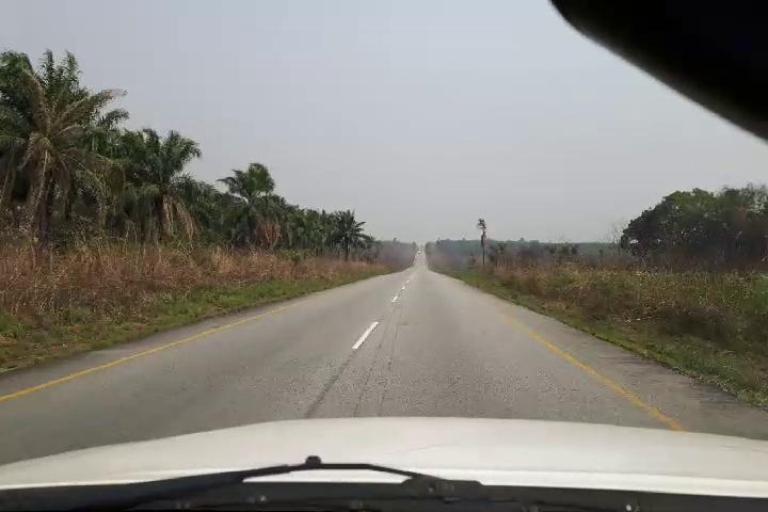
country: SL
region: Southern Province
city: Largo
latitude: 8.2359
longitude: -12.0824
